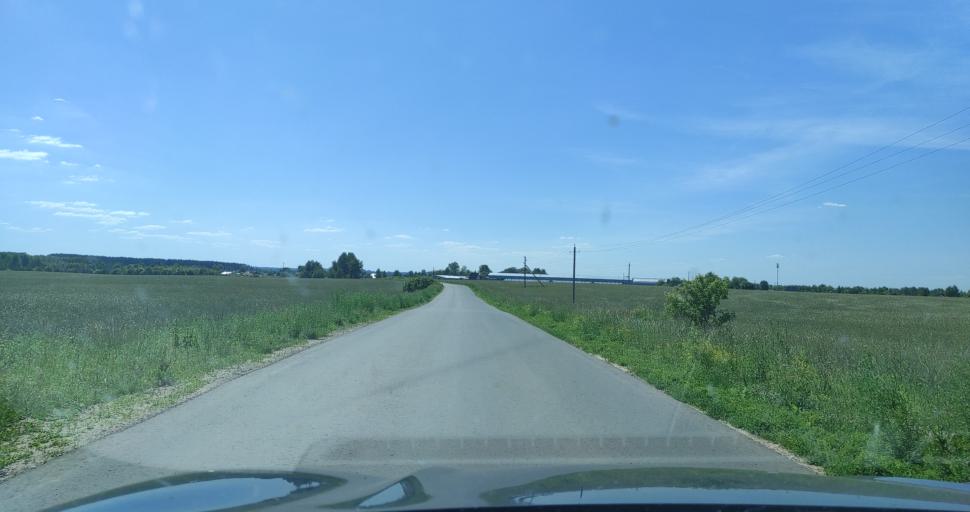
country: RU
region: Rjazan
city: Murmino
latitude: 54.5708
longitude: 40.1015
